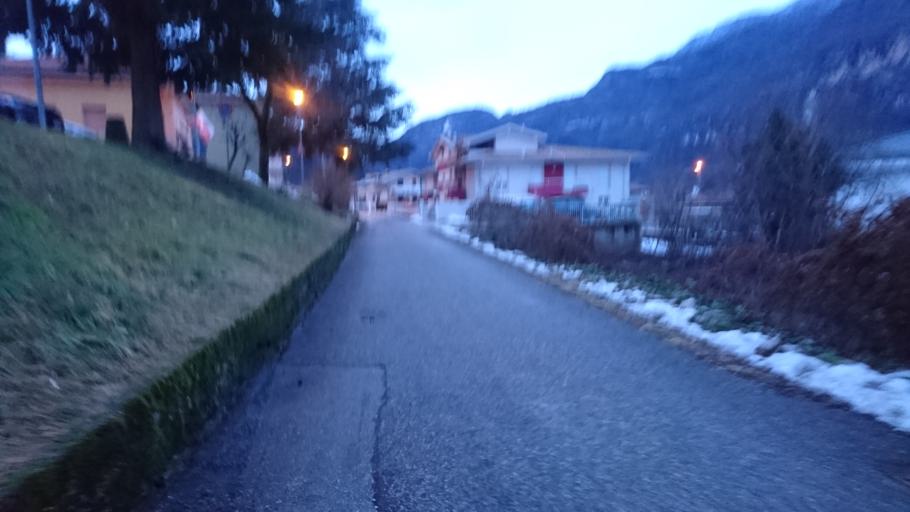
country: IT
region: Trentino-Alto Adige
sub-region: Provincia di Trento
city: Mori
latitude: 45.8444
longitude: 10.9856
